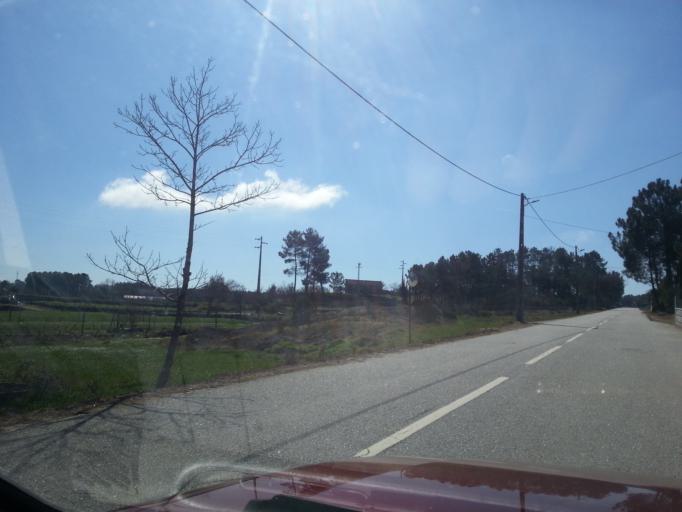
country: PT
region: Guarda
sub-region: Fornos de Algodres
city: Fornos de Algodres
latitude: 40.6466
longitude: -7.5319
